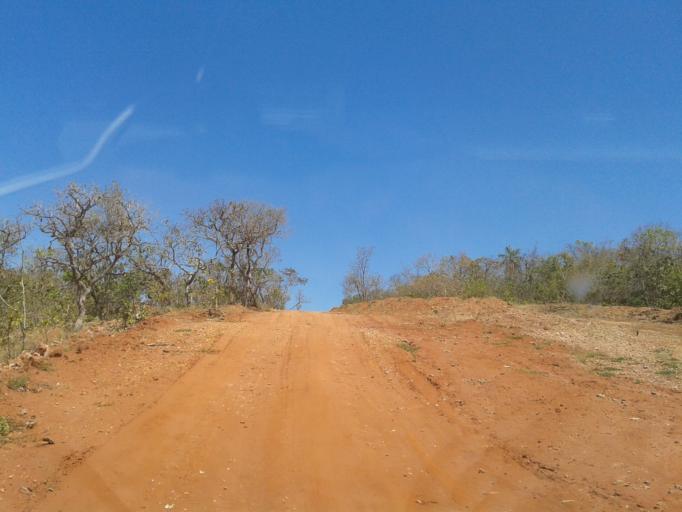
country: BR
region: Minas Gerais
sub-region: Ituiutaba
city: Ituiutaba
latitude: -19.1175
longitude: -49.2937
